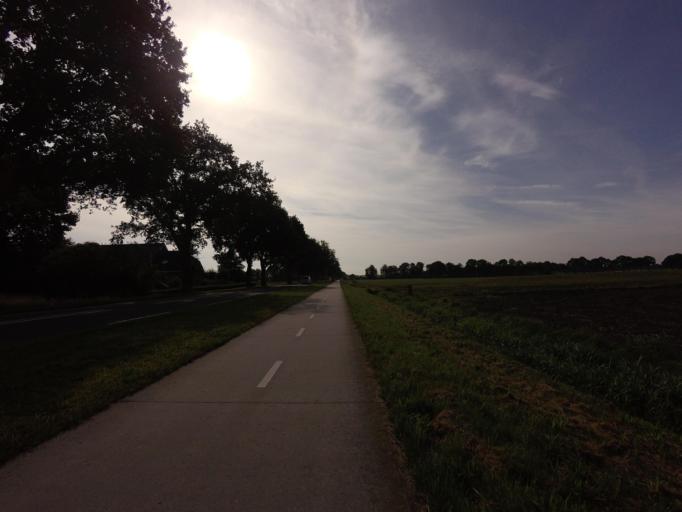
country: NL
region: Drenthe
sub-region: Gemeente Aa en Hunze
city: Anloo
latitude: 52.9525
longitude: 6.6657
